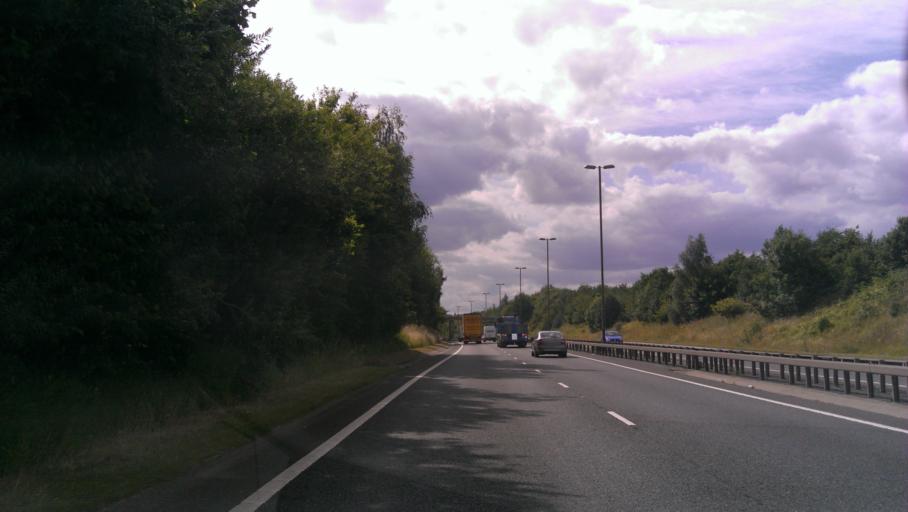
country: GB
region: England
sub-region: Kent
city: Strood
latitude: 51.4107
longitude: 0.4856
